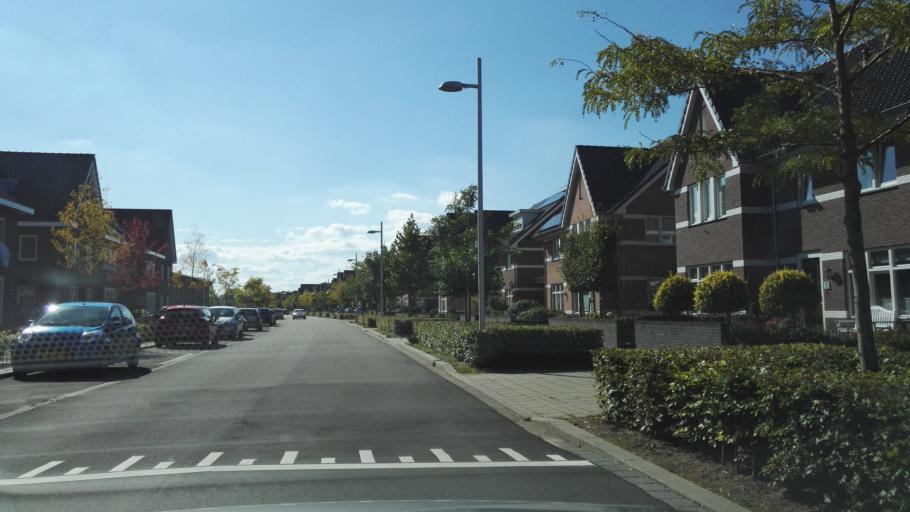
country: NL
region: Gelderland
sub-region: Gemeente Apeldoorn
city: Apeldoorn
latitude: 52.2378
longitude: 5.9980
